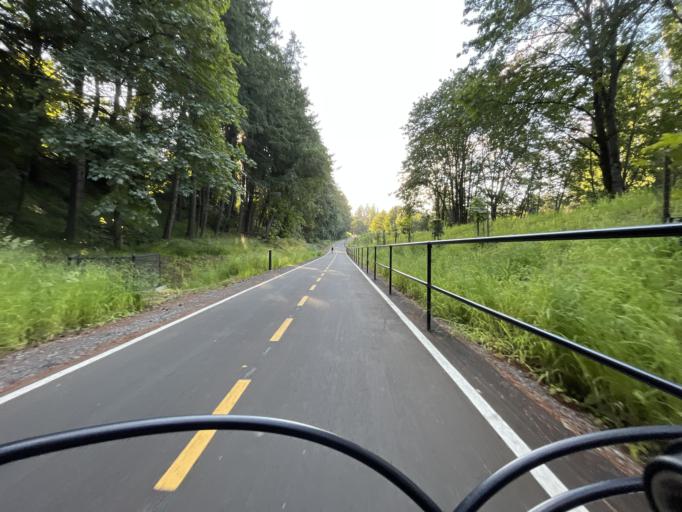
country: CA
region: British Columbia
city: Colwood
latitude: 48.4480
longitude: -123.4815
